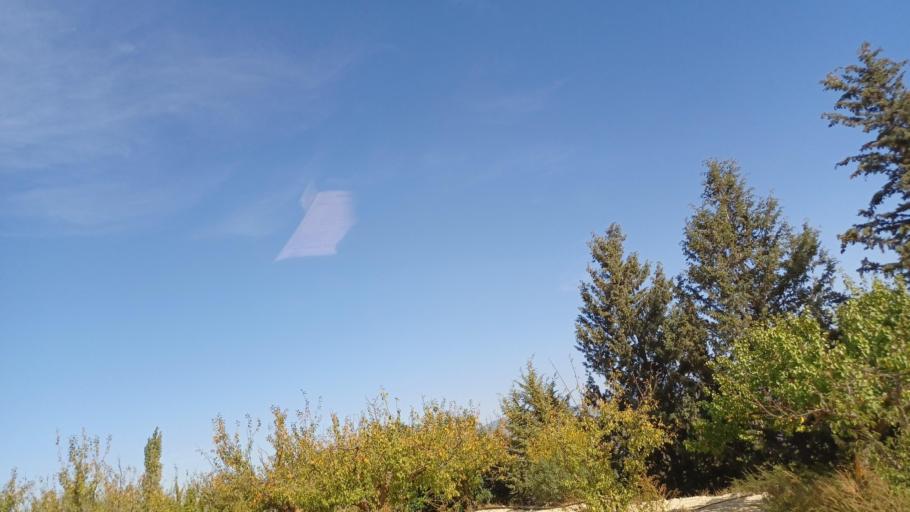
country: CY
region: Pafos
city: Pegeia
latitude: 34.9352
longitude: 32.4586
